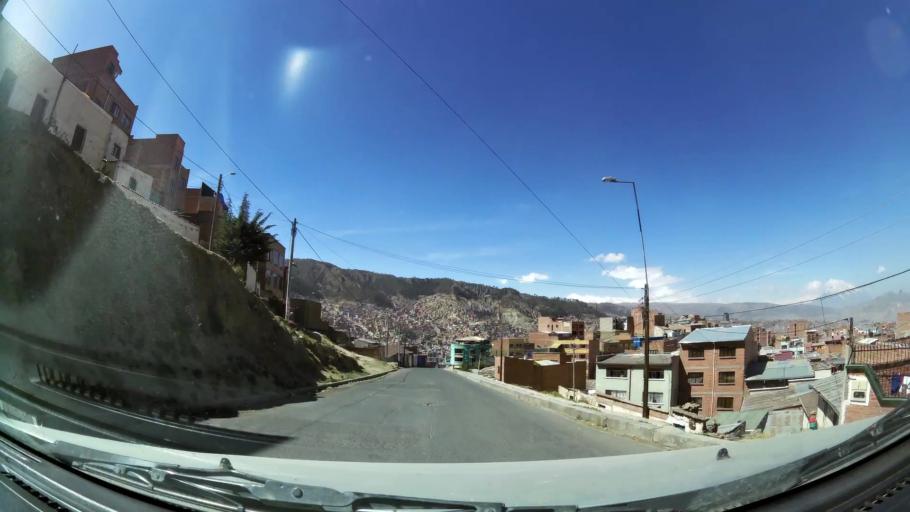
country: BO
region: La Paz
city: La Paz
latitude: -16.4889
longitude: -68.1533
